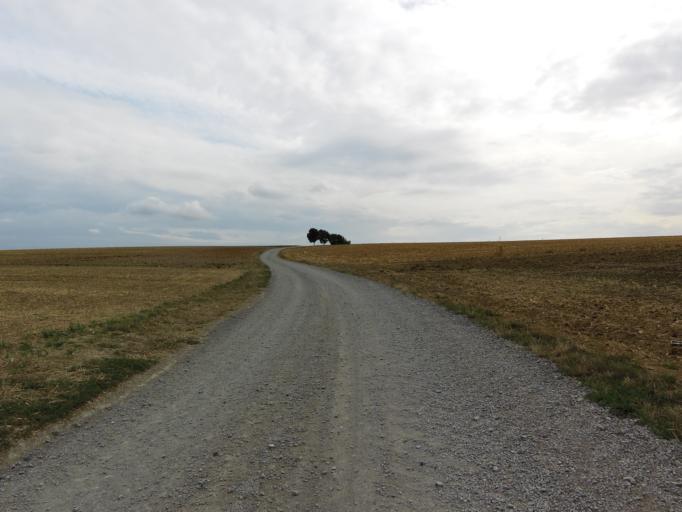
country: DE
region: Bavaria
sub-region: Regierungsbezirk Unterfranken
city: Rimpar
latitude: 49.8284
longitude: 9.9396
